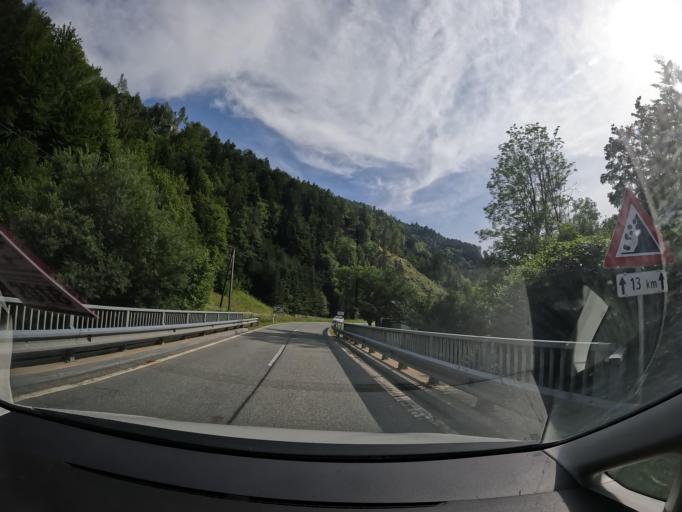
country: AT
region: Carinthia
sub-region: Politischer Bezirk Volkermarkt
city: Bad Eisenkappel
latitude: 46.4677
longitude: 14.5926
